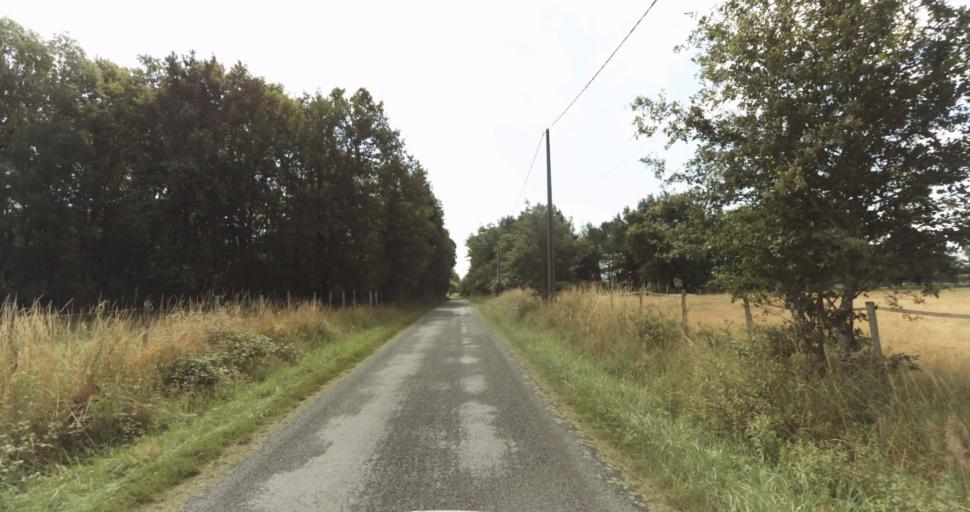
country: FR
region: Aquitaine
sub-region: Departement de la Gironde
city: Bazas
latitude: 44.4547
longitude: -0.1901
